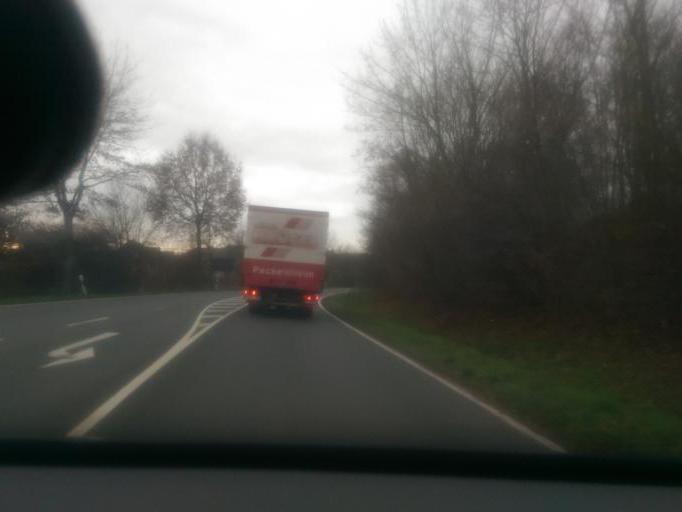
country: DE
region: North Rhine-Westphalia
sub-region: Regierungsbezirk Detmold
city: Delbruck
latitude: 51.7685
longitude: 8.5774
